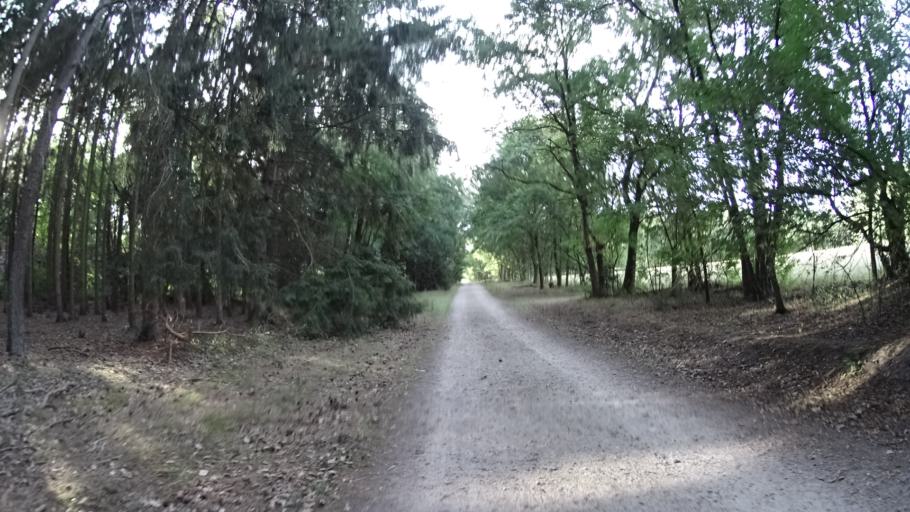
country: DE
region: Lower Saxony
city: Handeloh
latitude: 53.2121
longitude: 9.8814
